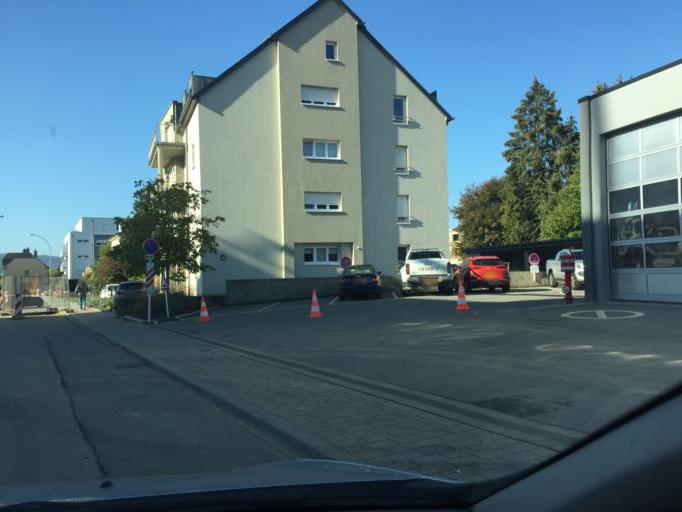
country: LU
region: Diekirch
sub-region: Canton de Diekirch
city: Diekirch
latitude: 49.8658
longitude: 6.1532
